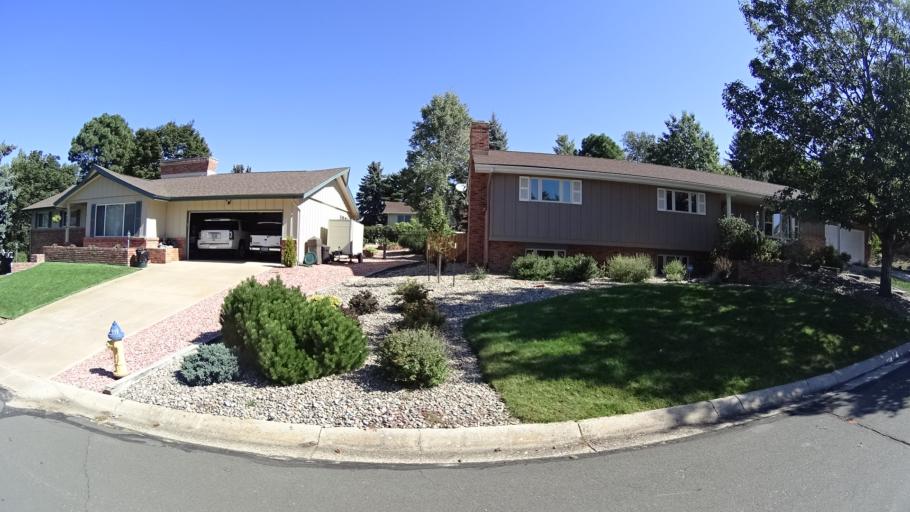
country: US
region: Colorado
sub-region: El Paso County
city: Colorado Springs
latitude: 38.8742
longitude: -104.7812
